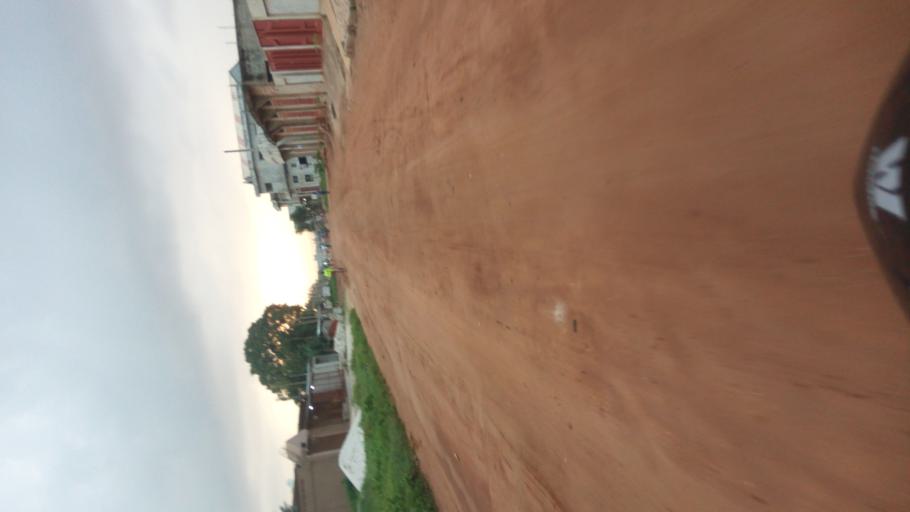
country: BJ
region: Atlantique
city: Abomey-Calavi
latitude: 6.4388
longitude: 2.3164
